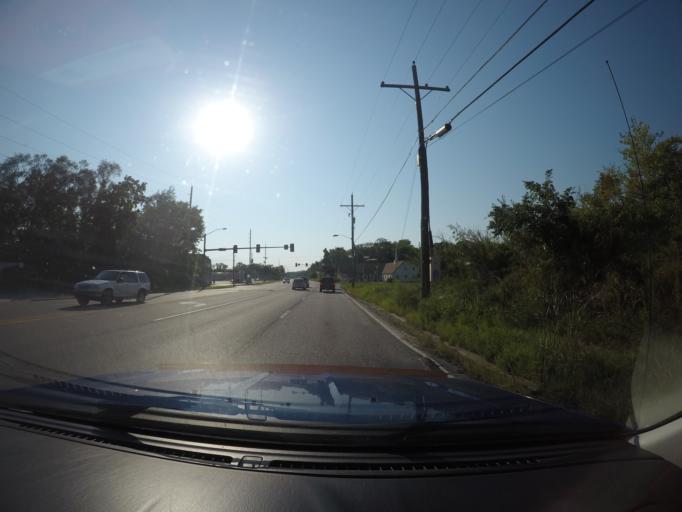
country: US
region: Kansas
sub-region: Wyandotte County
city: Edwardsville
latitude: 39.0623
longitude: -94.8207
